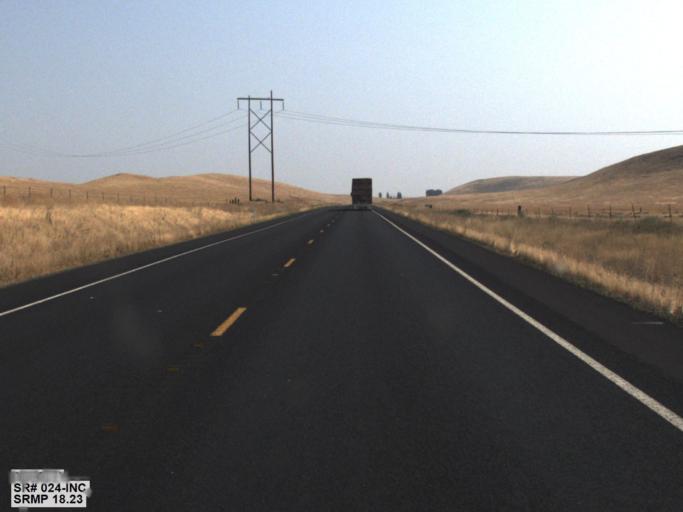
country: US
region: Washington
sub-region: Yakima County
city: Zillah
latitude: 46.5019
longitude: -120.1284
